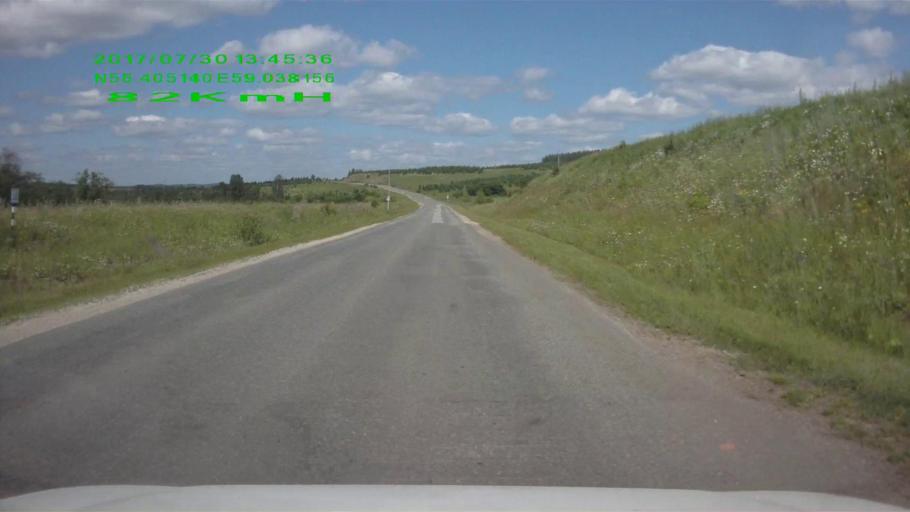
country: RU
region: Sverdlovsk
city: Mikhaylovsk
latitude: 56.4060
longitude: 59.0397
